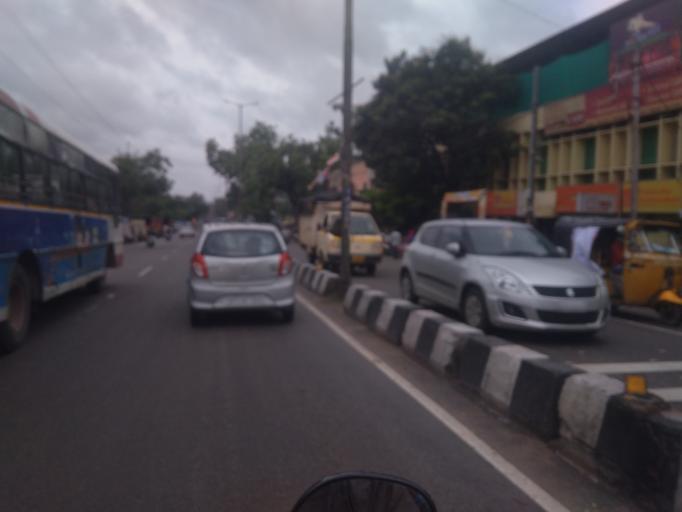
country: IN
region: Telangana
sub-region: Rangareddi
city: Secunderabad
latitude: 17.5017
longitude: 78.5140
